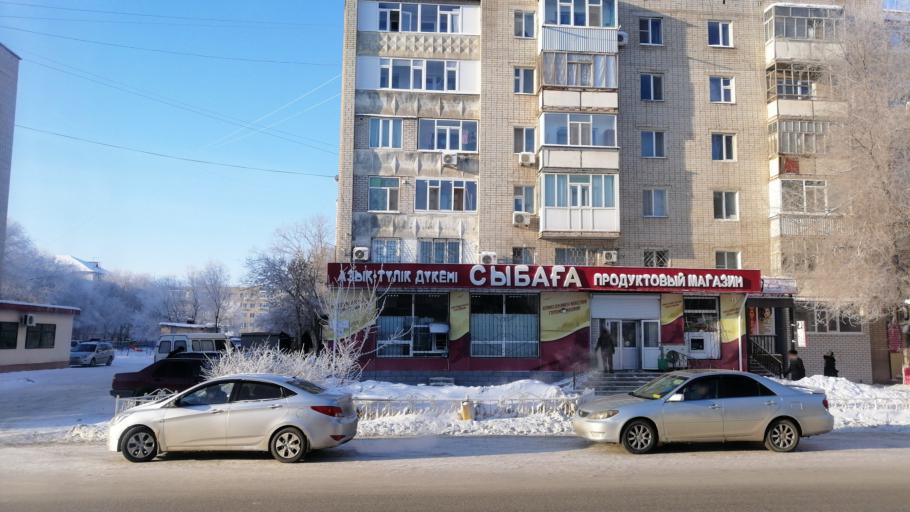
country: KZ
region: Aqtoebe
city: Aqtobe
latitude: 50.2930
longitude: 57.1492
